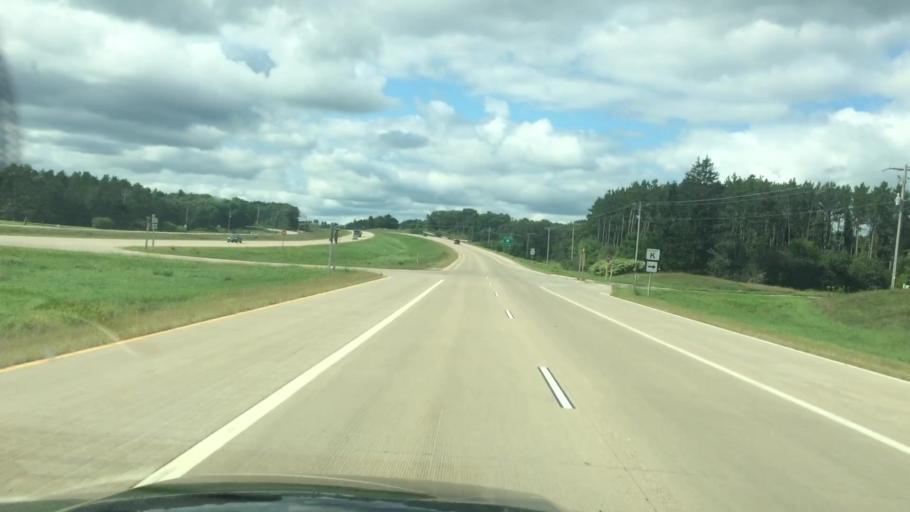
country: US
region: Wisconsin
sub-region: Portage County
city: Plover
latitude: 44.5131
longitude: -89.4255
